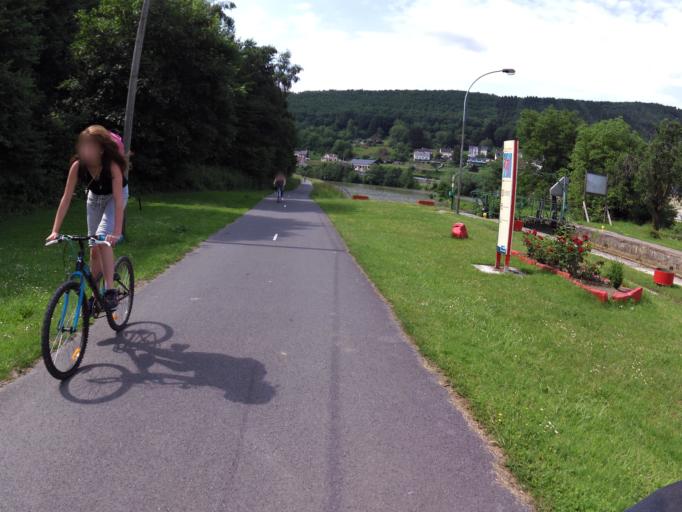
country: FR
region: Champagne-Ardenne
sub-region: Departement des Ardennes
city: Montherme
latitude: 49.8595
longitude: 4.7523
